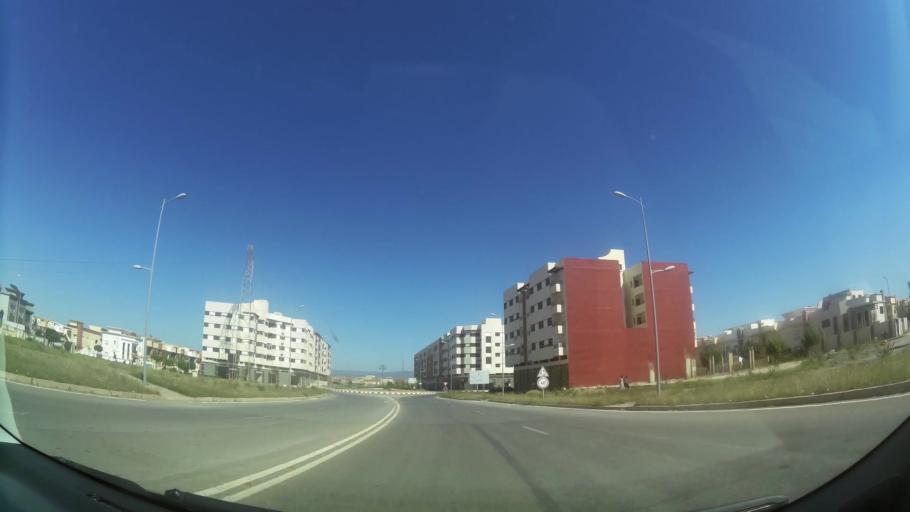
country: MA
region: Oriental
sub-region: Oujda-Angad
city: Oujda
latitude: 34.7235
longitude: -1.9111
